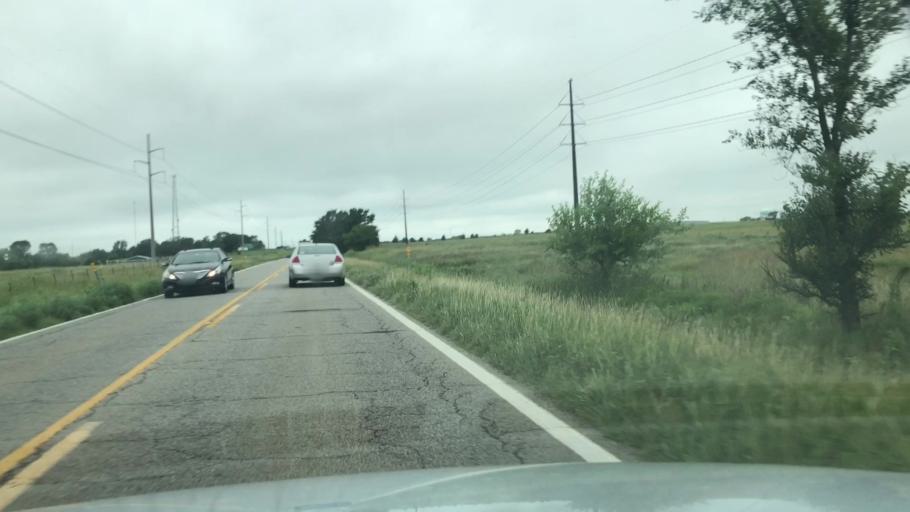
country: US
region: Oklahoma
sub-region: Washington County
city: Dewey
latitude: 36.7280
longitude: -95.8834
